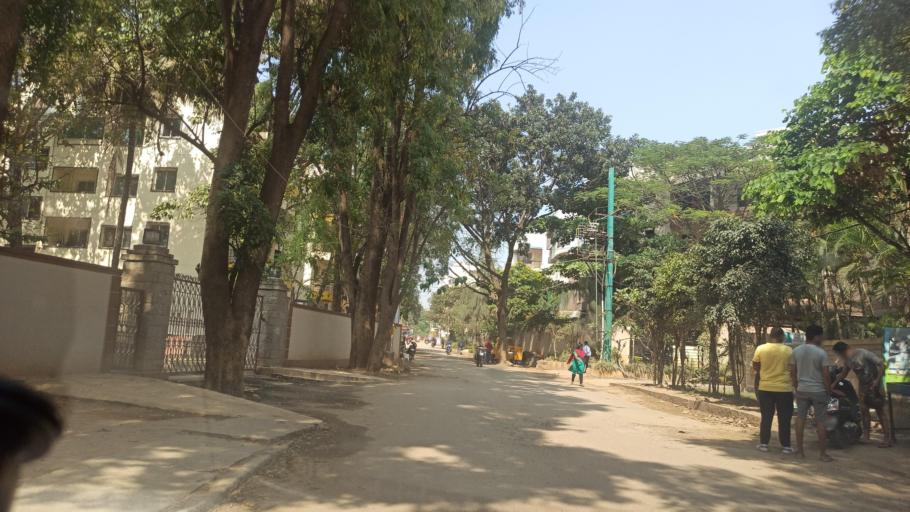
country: IN
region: Karnataka
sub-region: Bangalore Urban
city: Bangalore
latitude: 12.9528
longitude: 77.7060
